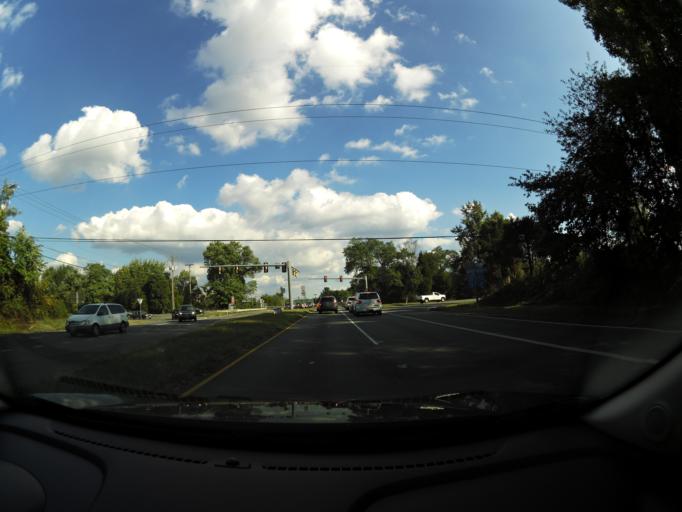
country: US
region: Virginia
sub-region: Fairfax County
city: McLean
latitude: 38.9550
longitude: -77.1953
